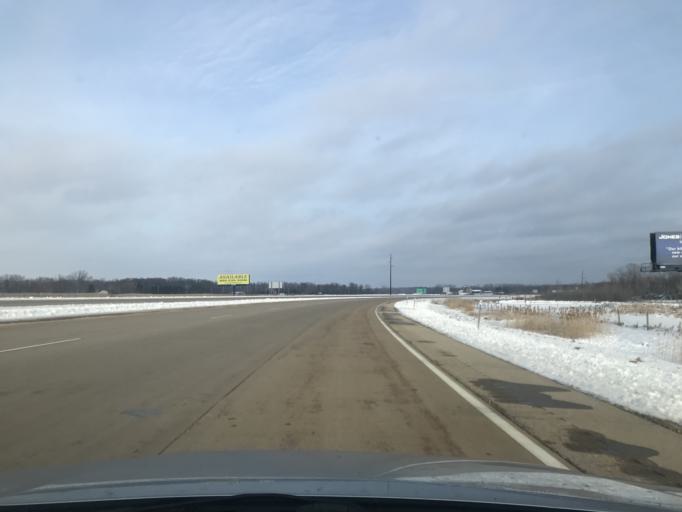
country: US
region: Wisconsin
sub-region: Oconto County
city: Oconto
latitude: 44.9005
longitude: -87.8974
